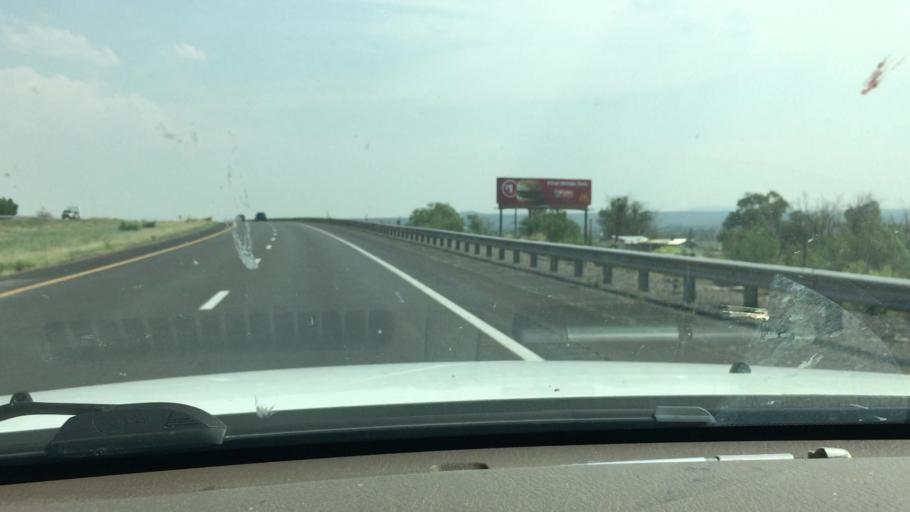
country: US
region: New Mexico
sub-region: Cibola County
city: Milan
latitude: 35.1720
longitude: -107.9002
